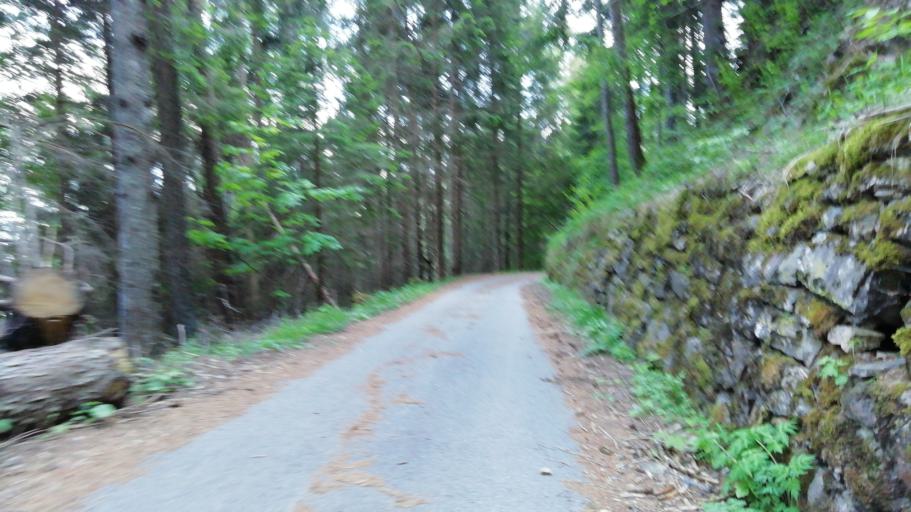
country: IT
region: Veneto
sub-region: Provincia di Belluno
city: Valle di Cadore
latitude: 46.4253
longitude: 12.3232
